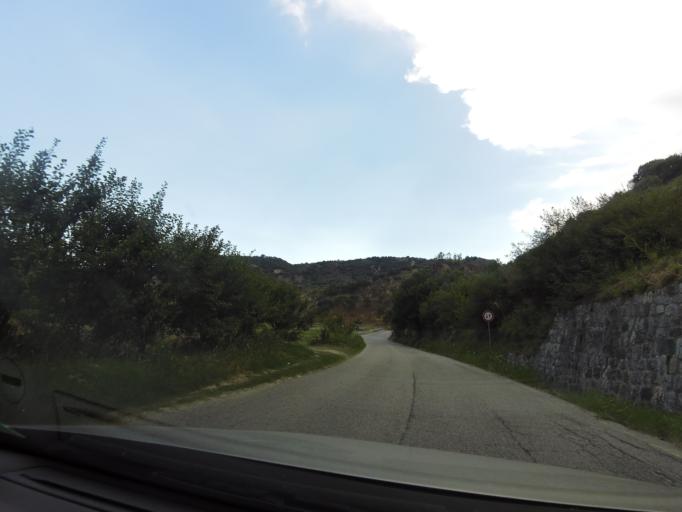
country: IT
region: Calabria
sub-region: Provincia di Reggio Calabria
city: Stilo
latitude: 38.4694
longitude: 16.4850
